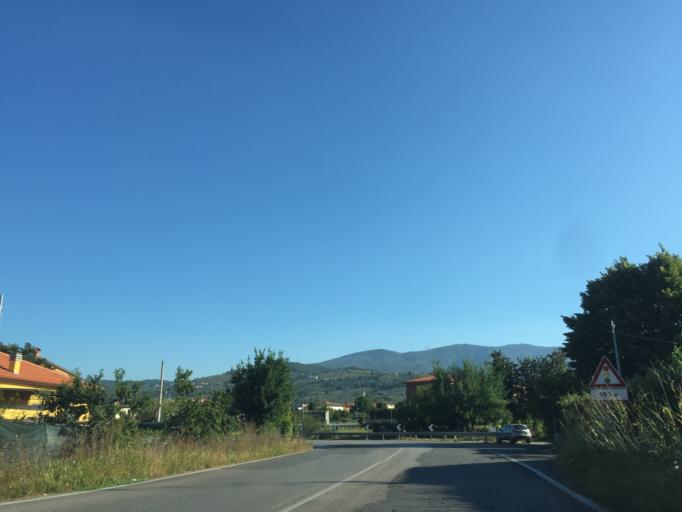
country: IT
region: Tuscany
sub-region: Provincia di Pistoia
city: Pistoia
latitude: 43.9458
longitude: 10.9355
